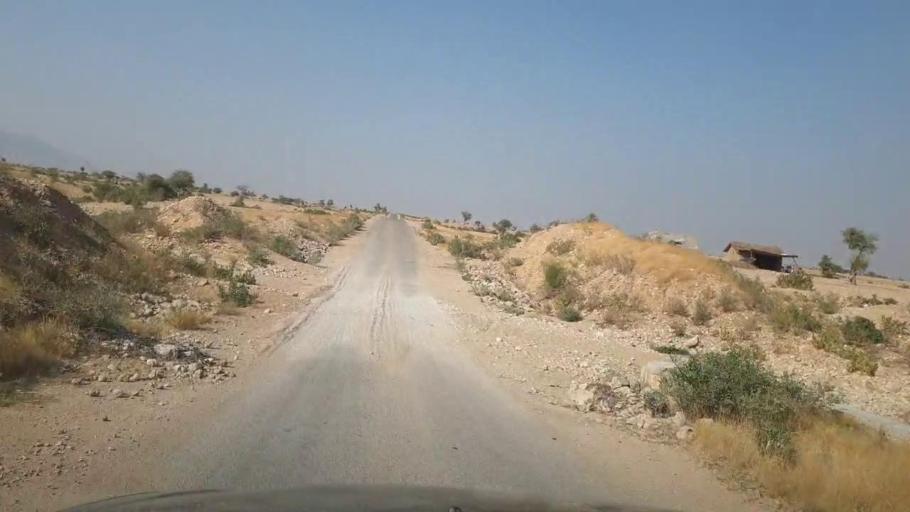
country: PK
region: Sindh
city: Jamshoro
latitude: 25.5978
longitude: 67.8168
